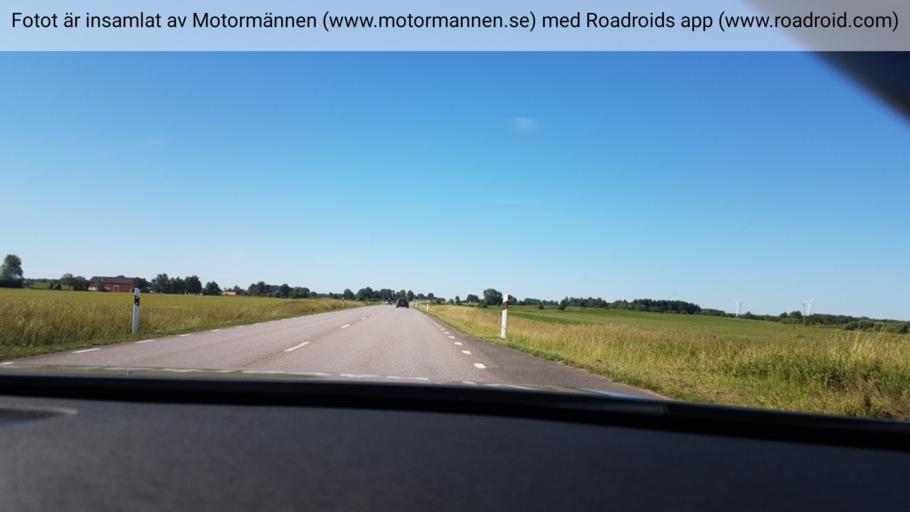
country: SE
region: Vaestra Goetaland
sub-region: Falkopings Kommun
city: Falkoeping
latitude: 58.1194
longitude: 13.5452
